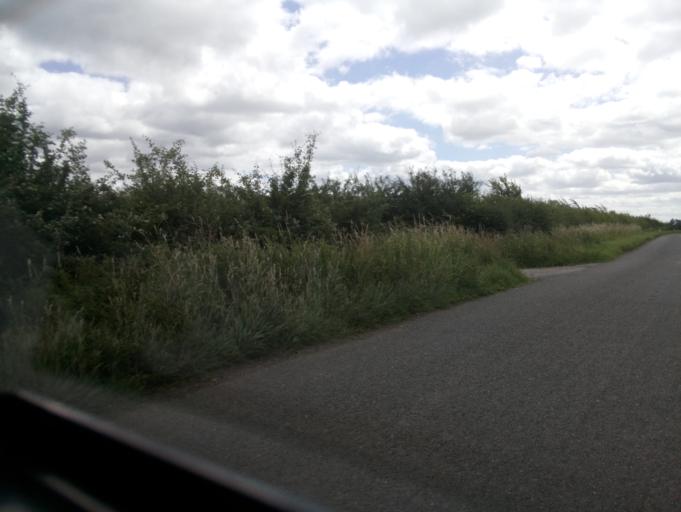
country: GB
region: England
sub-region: Nottinghamshire
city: Ruddington
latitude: 52.8458
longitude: -1.1030
